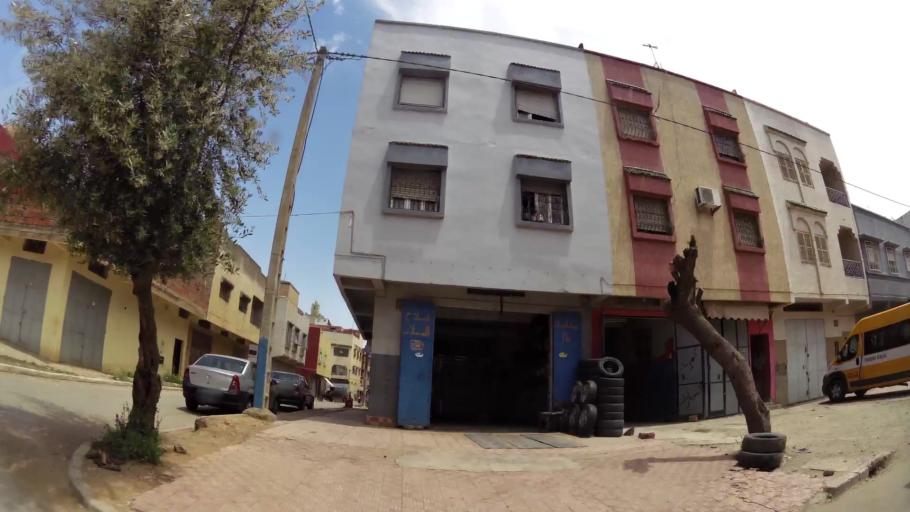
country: MA
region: Rabat-Sale-Zemmour-Zaer
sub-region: Khemisset
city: Khemisset
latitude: 33.8245
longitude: -6.0772
